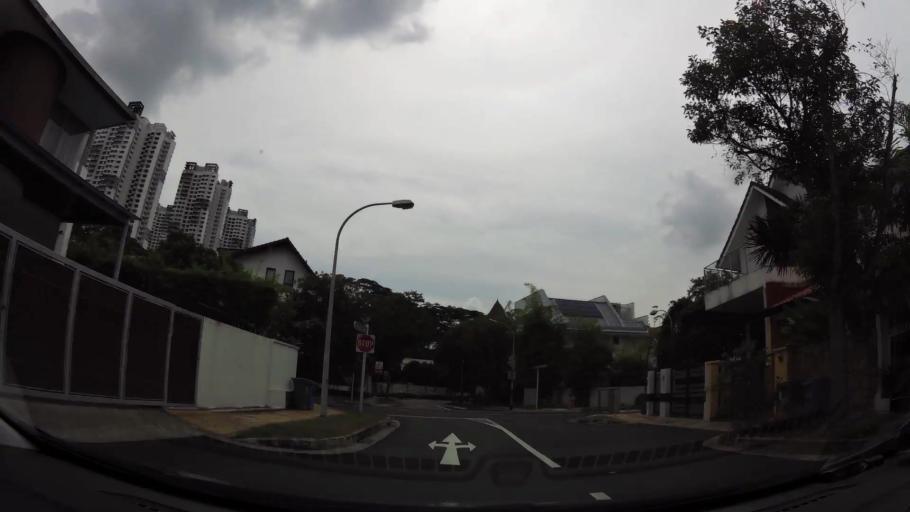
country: SG
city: Singapore
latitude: 1.3122
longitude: 103.7842
